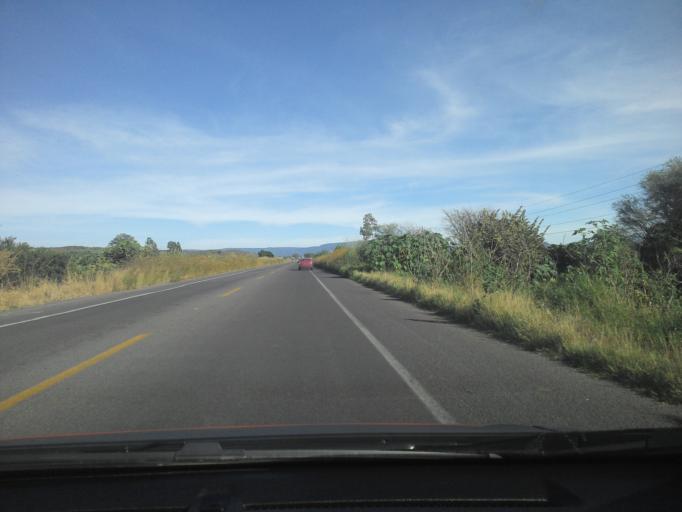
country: MX
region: Jalisco
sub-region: Teuchitlan
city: La Estanzuela
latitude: 20.6710
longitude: -103.8119
